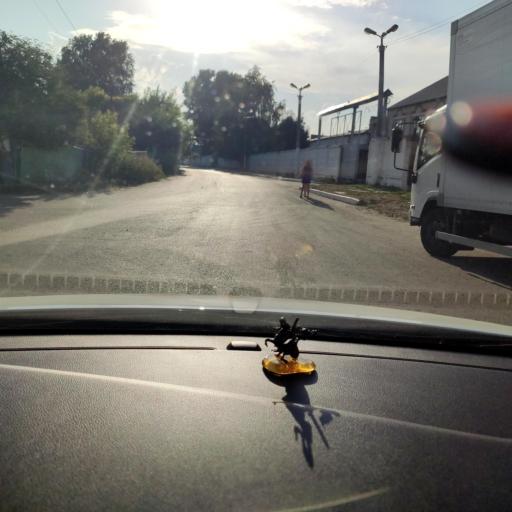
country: RU
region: Tatarstan
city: Staroye Arakchino
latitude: 55.8149
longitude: 48.9087
